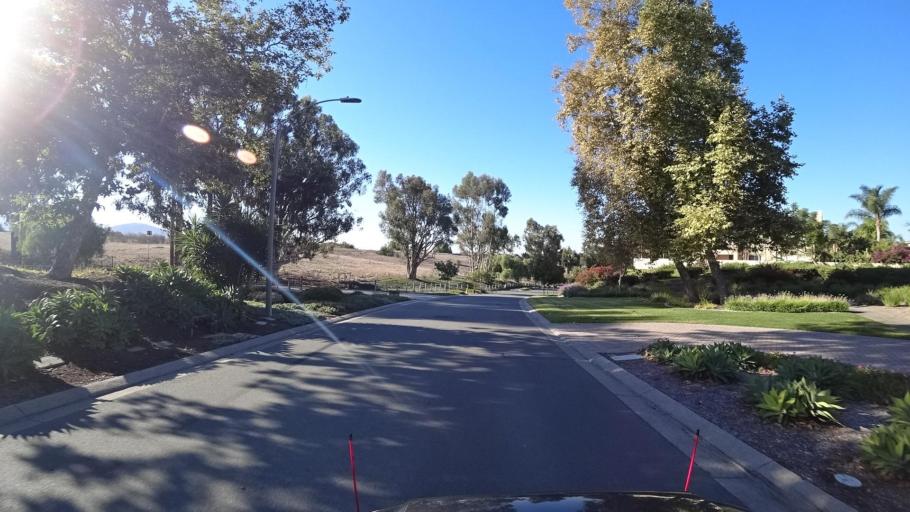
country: US
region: California
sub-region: San Diego County
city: La Presa
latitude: 32.6485
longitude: -116.9427
